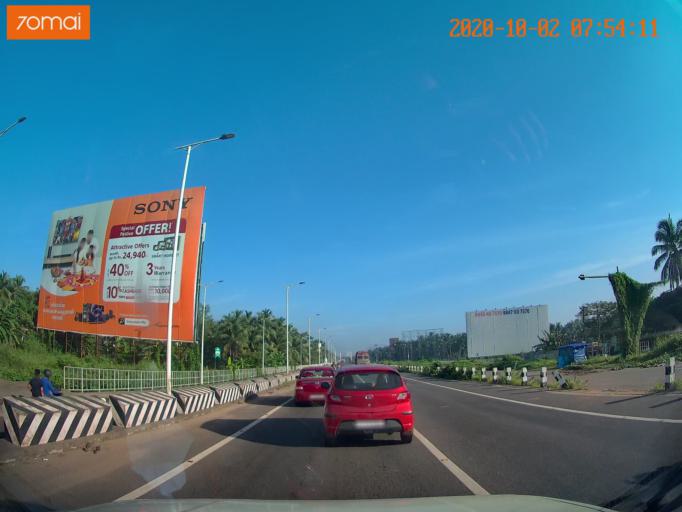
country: IN
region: Kerala
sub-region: Kozhikode
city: Ferokh
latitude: 11.1704
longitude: 75.8749
